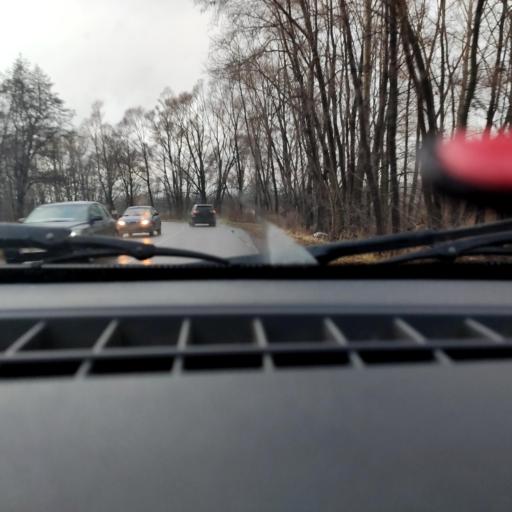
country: RU
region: Bashkortostan
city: Avdon
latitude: 54.5104
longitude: 55.8683
